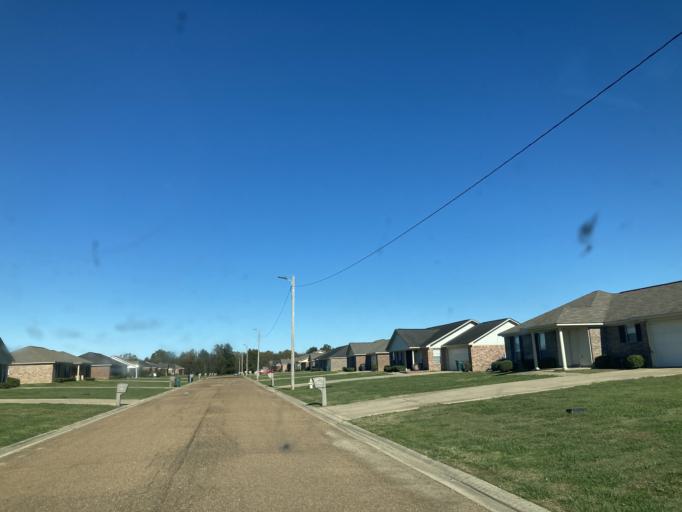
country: US
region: Mississippi
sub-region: Yazoo County
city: Yazoo City
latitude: 32.8567
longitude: -90.4278
